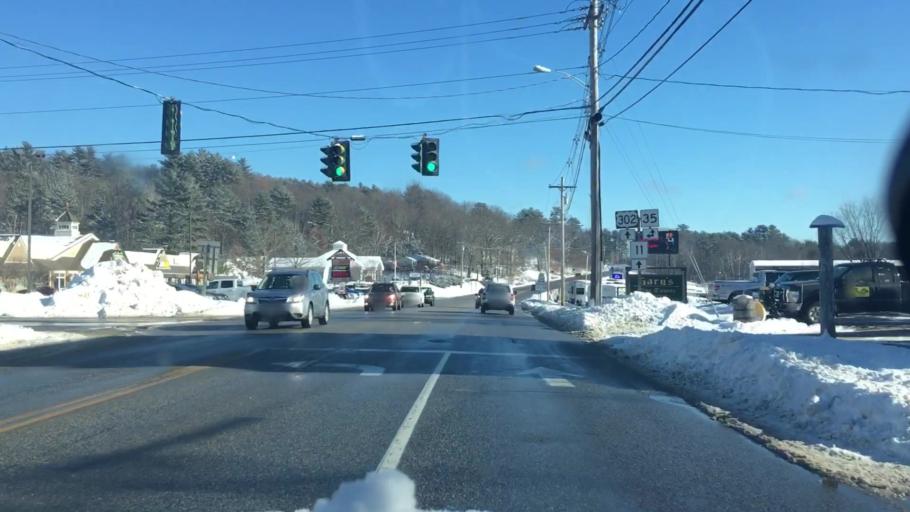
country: US
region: Maine
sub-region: Cumberland County
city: Raymond
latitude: 43.9697
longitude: -70.5944
